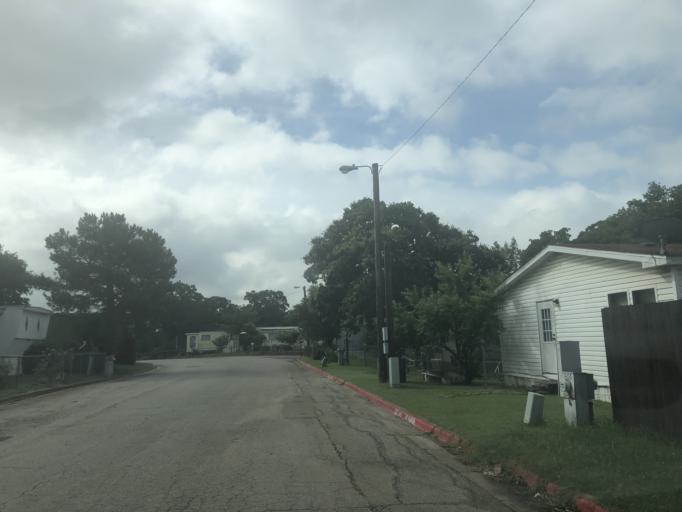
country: US
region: Texas
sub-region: Dallas County
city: Irving
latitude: 32.8112
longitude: -96.9974
